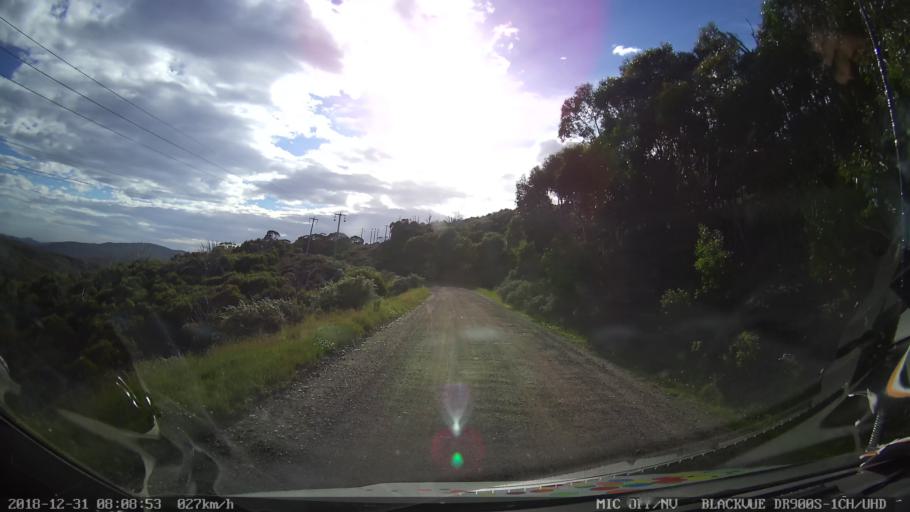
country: AU
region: New South Wales
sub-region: Snowy River
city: Jindabyne
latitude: -36.3810
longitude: 148.4148
